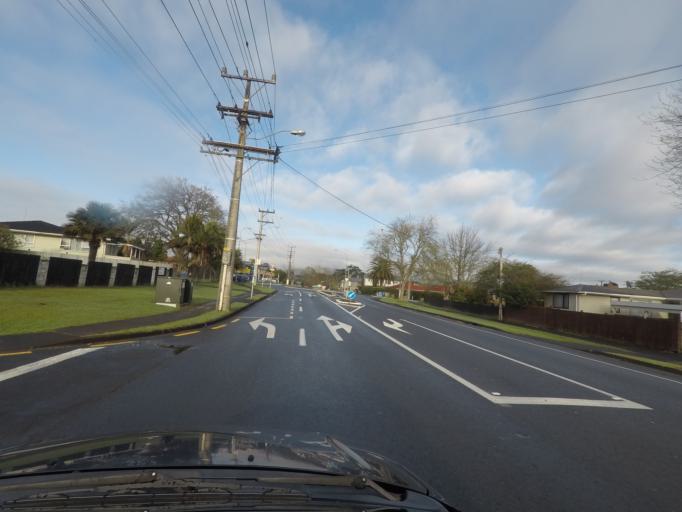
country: NZ
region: Auckland
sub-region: Auckland
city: Waitakere
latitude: -36.8931
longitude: 174.6205
